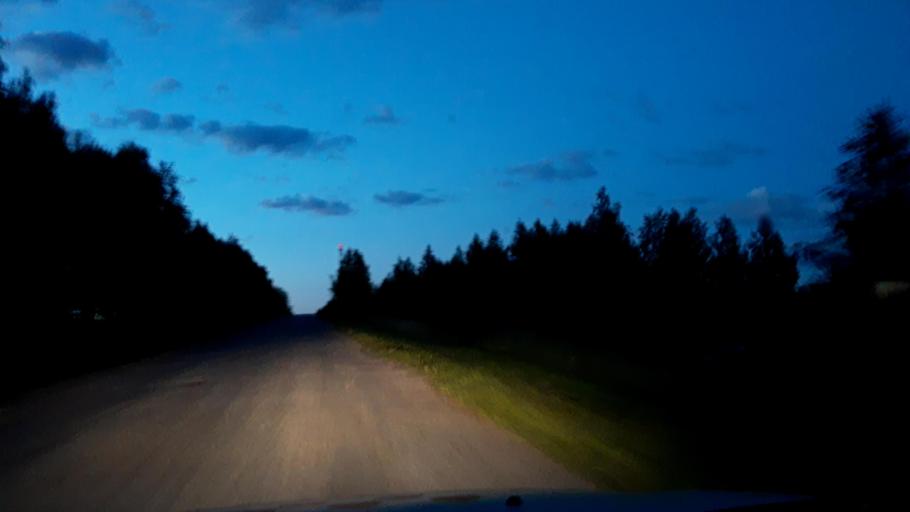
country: RU
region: Nizjnij Novgorod
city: Pamyat' Parizhskoy Kommuny
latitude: 56.0515
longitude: 44.4420
